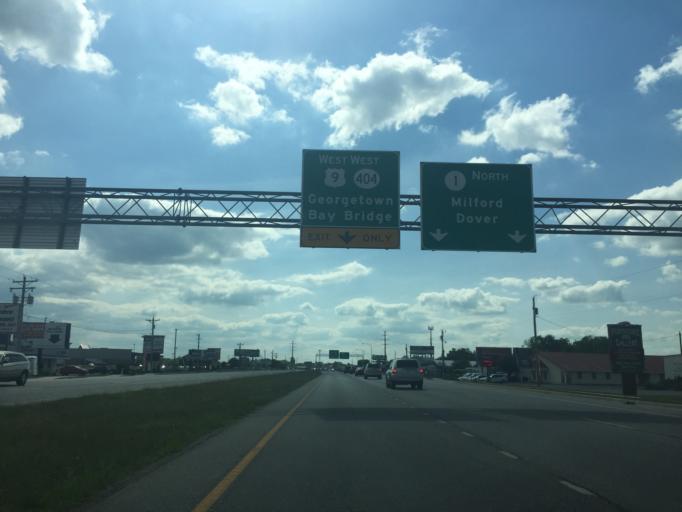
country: US
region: Delaware
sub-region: Sussex County
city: Lewes
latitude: 38.7486
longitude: -75.1670
